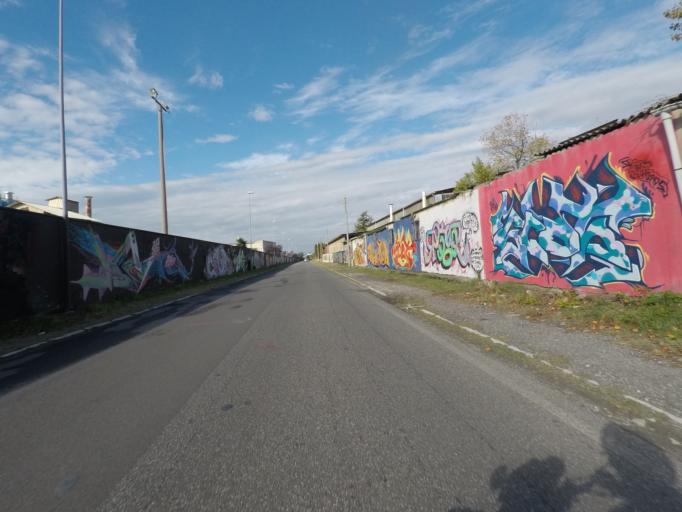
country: IT
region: Tuscany
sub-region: Provincia di Massa-Carrara
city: Massa
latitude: 44.0304
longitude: 10.1086
